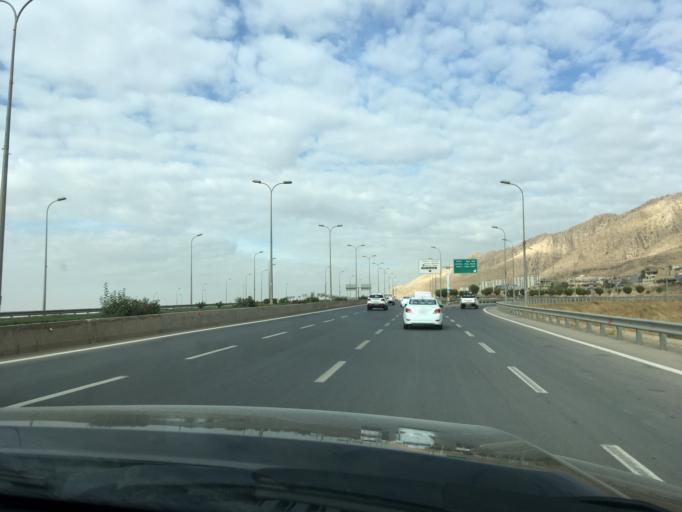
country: IQ
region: Dahuk
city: Sinah
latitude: 36.8493
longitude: 43.0542
